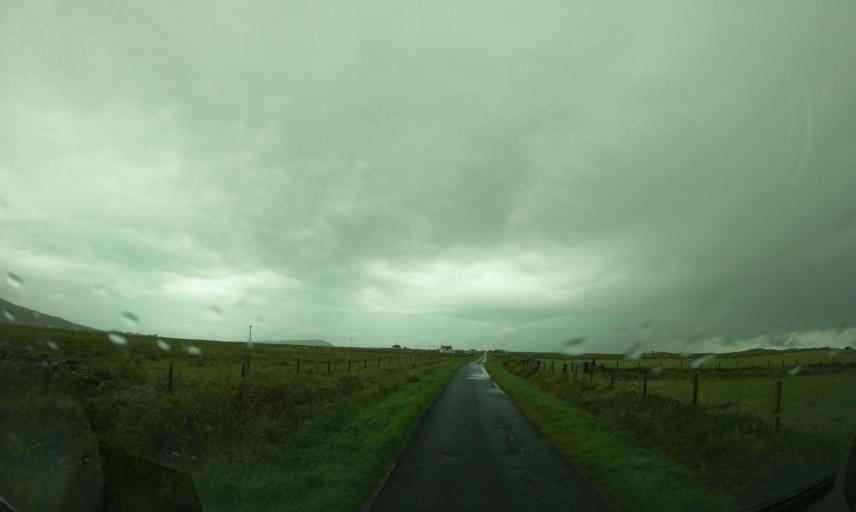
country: GB
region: Scotland
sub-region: Eilean Siar
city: Barra
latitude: 56.4736
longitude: -6.9101
